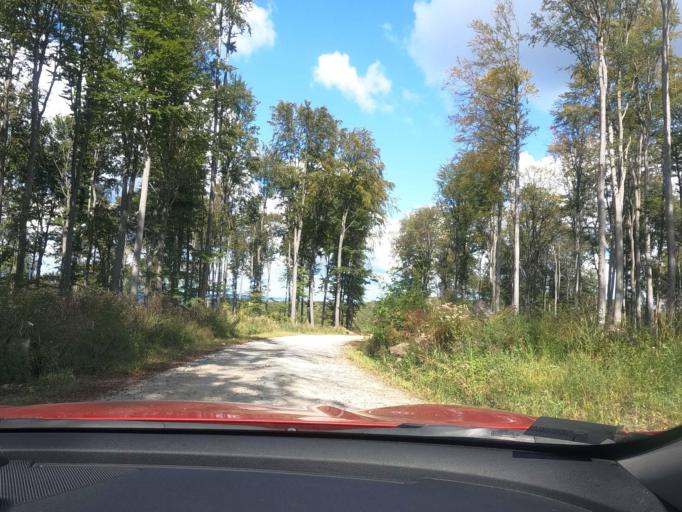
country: HR
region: Karlovacka
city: Vojnic
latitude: 45.2917
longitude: 15.7837
